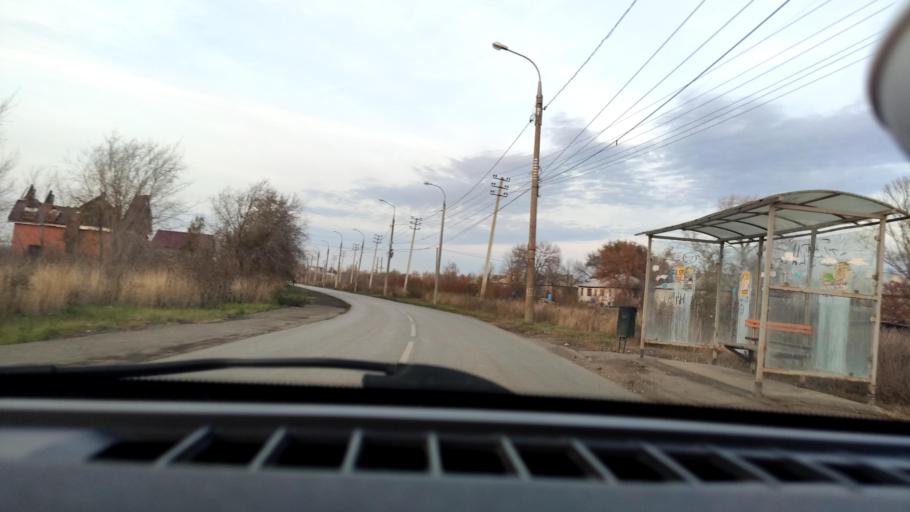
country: RU
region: Samara
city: Samara
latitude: 53.1423
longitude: 50.1323
